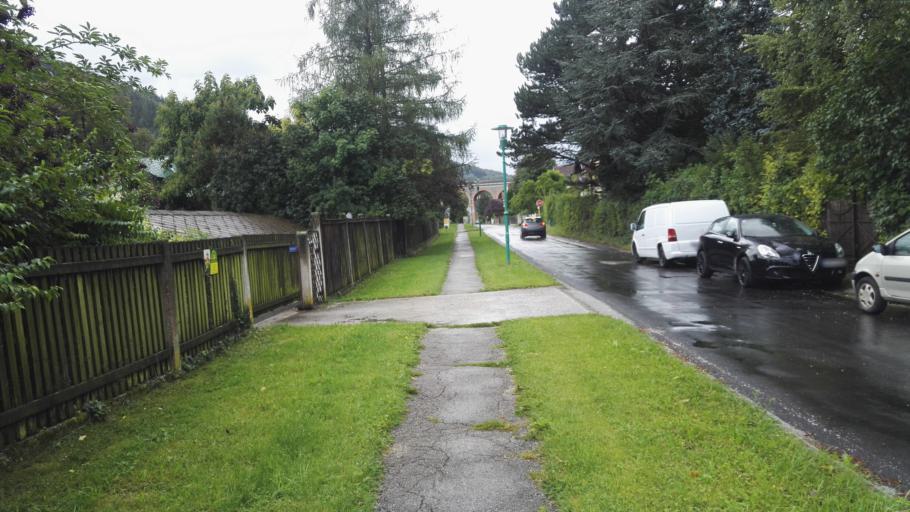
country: AT
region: Lower Austria
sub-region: Politischer Bezirk Neunkirchen
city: Payerbach
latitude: 47.6936
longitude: 15.8612
